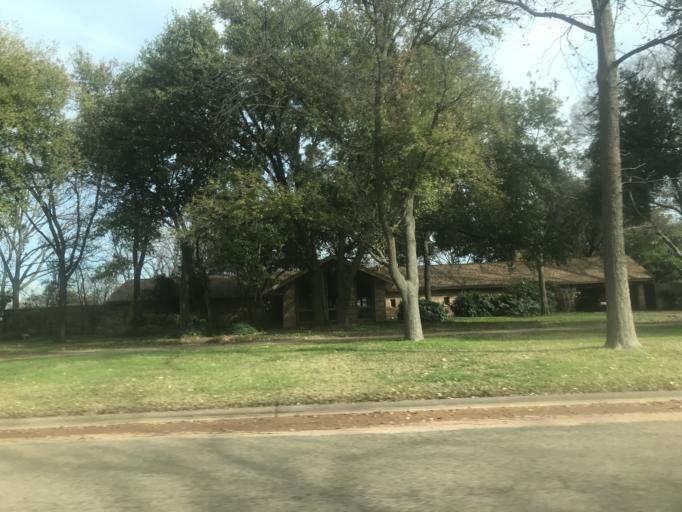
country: US
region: Texas
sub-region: Taylor County
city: Abilene
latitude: 32.4273
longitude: -99.7710
